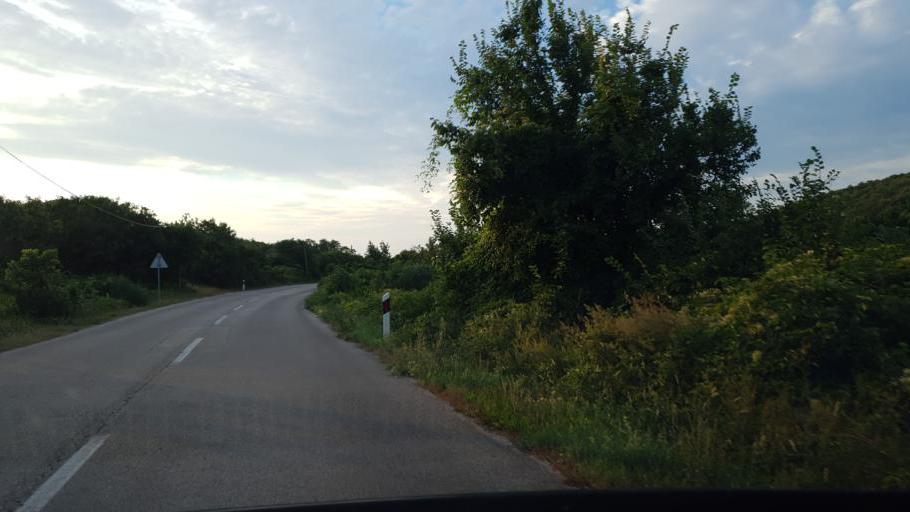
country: HR
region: Primorsko-Goranska
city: Punat
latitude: 44.9980
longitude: 14.6359
